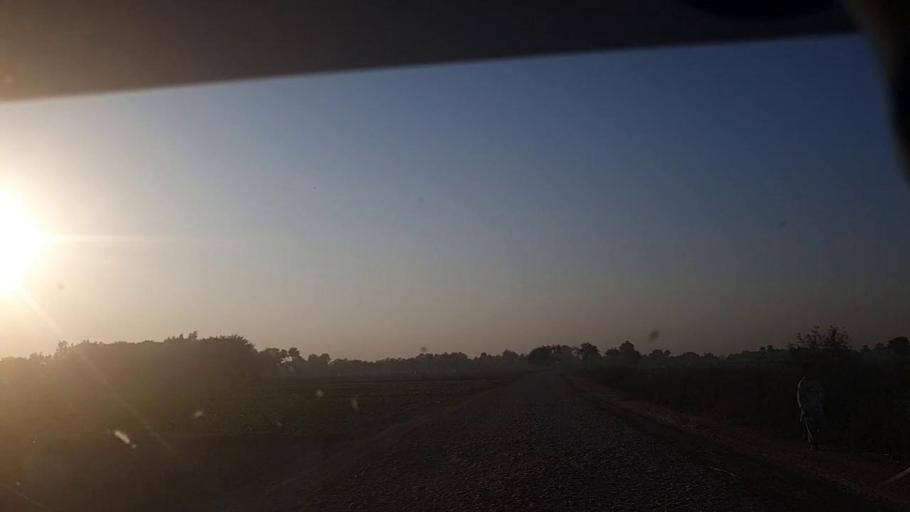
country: PK
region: Sindh
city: Sobhadero
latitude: 27.3613
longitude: 68.4175
